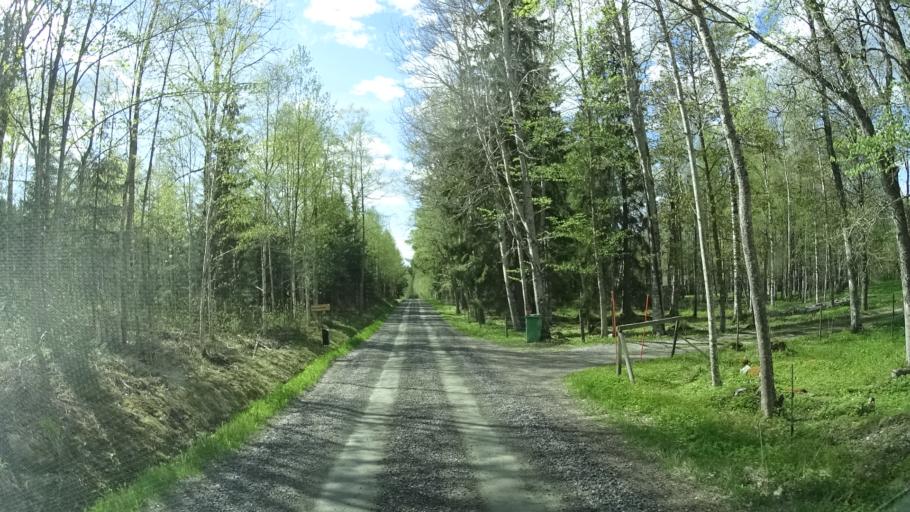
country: SE
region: OErebro
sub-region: Nora Kommun
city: As
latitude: 59.4412
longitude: 14.8423
